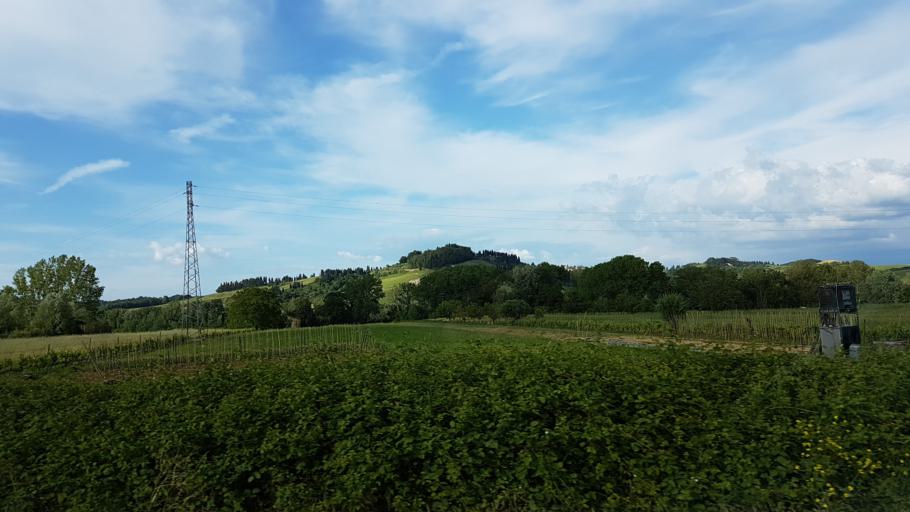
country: IT
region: Tuscany
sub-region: Province of Pisa
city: Lajatico
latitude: 43.4927
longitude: 10.7377
